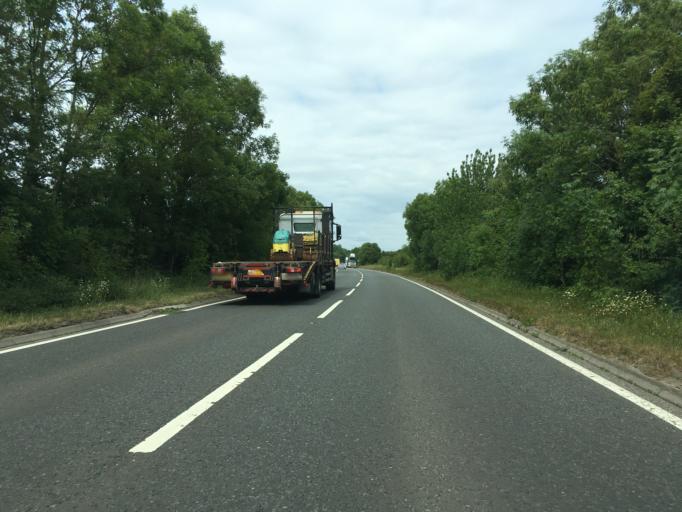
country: GB
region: England
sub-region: South Gloucestershire
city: Severn Beach
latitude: 51.5946
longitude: -2.6227
